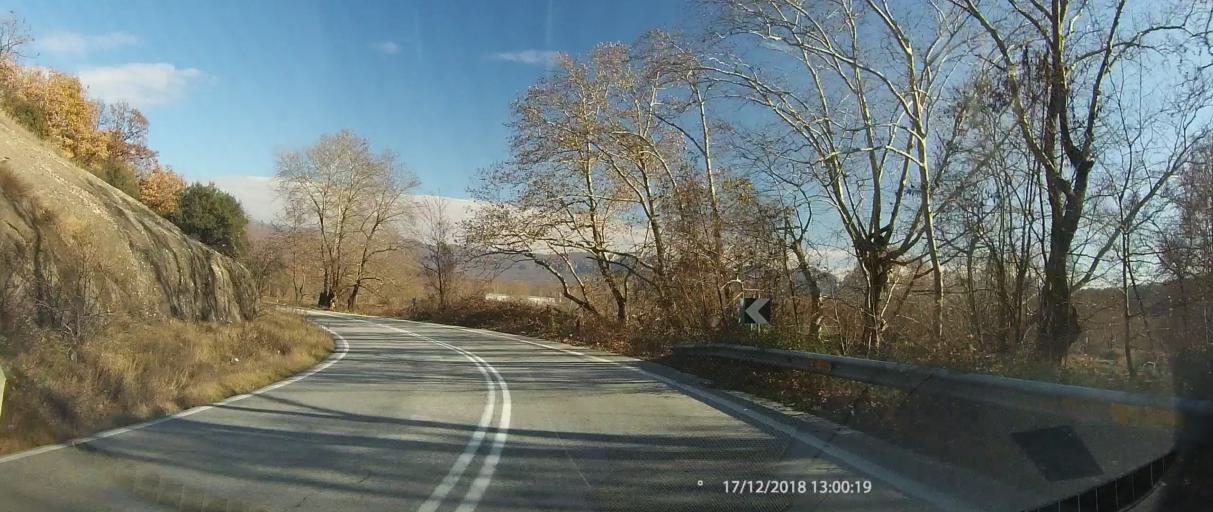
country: GR
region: Thessaly
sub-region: Trikala
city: Kastraki
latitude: 39.7292
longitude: 21.5654
